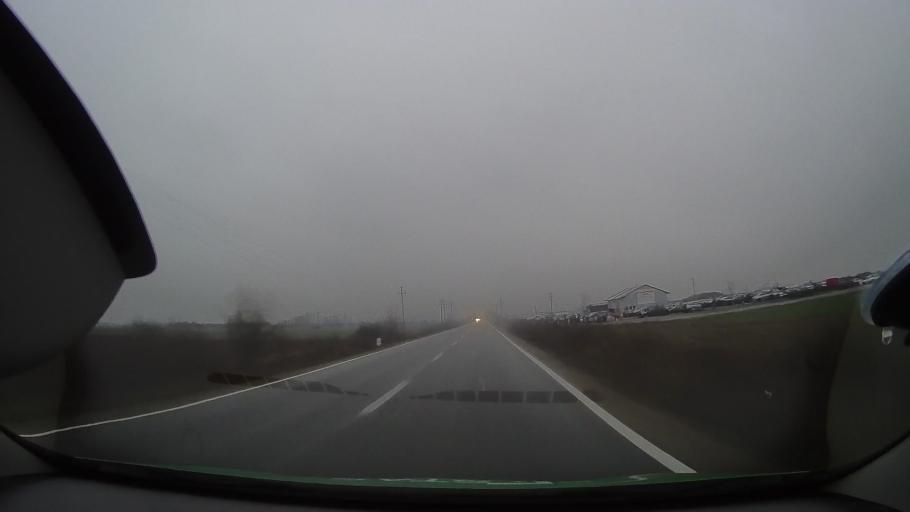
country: RO
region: Bihor
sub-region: Comuna Tinca
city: Tinca
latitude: 46.7658
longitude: 21.9335
